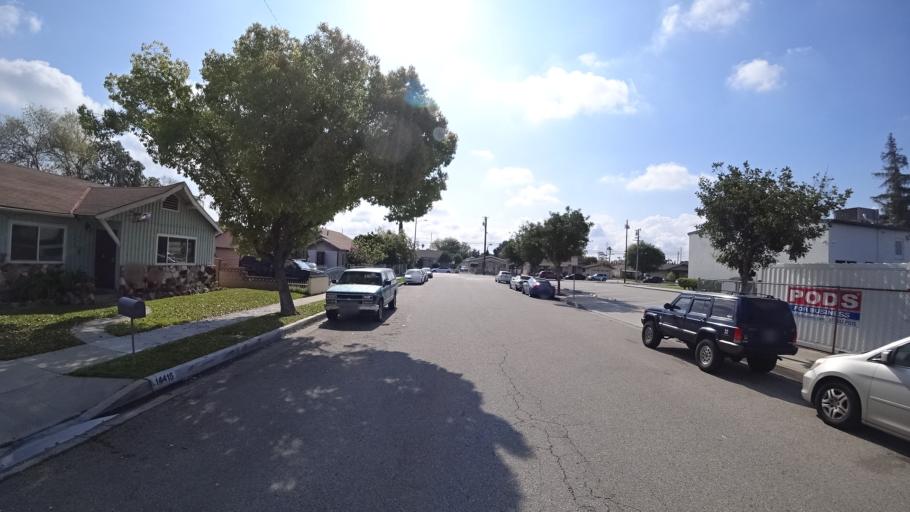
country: US
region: California
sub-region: Los Angeles County
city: Baldwin Park
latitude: 34.0804
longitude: -117.9606
